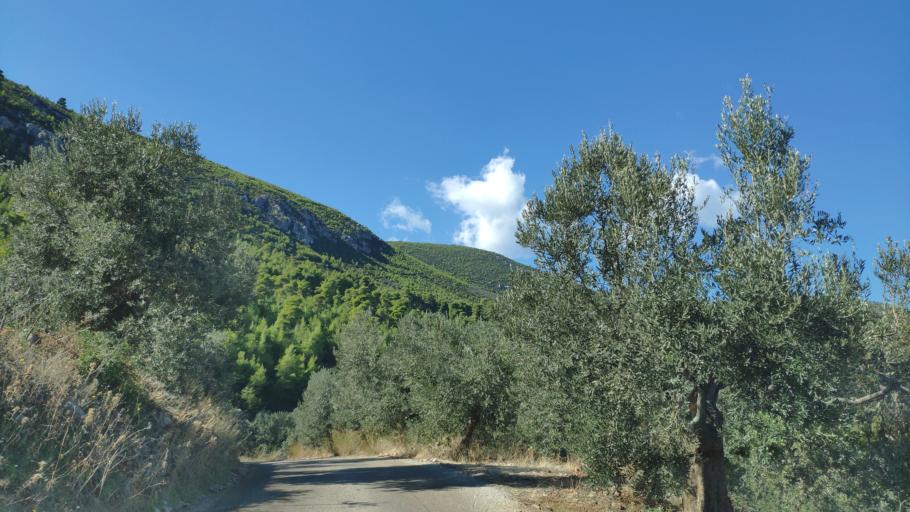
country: GR
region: Peloponnese
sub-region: Nomos Korinthias
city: Sofikon
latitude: 37.7342
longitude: 23.1056
